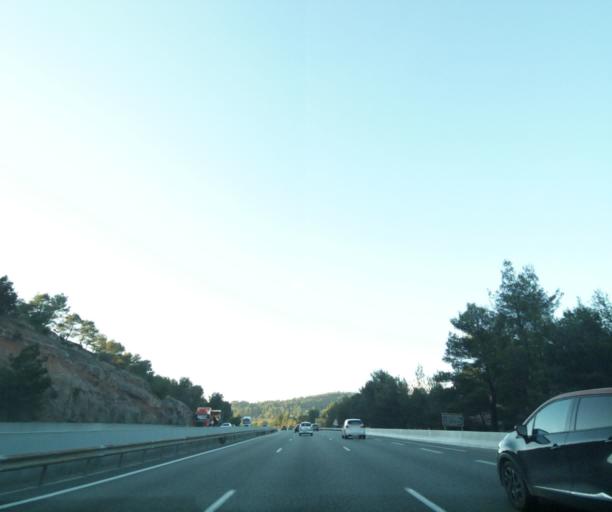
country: FR
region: Provence-Alpes-Cote d'Azur
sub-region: Departement des Bouches-du-Rhone
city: Le Tholonet
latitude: 43.4997
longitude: 5.5227
